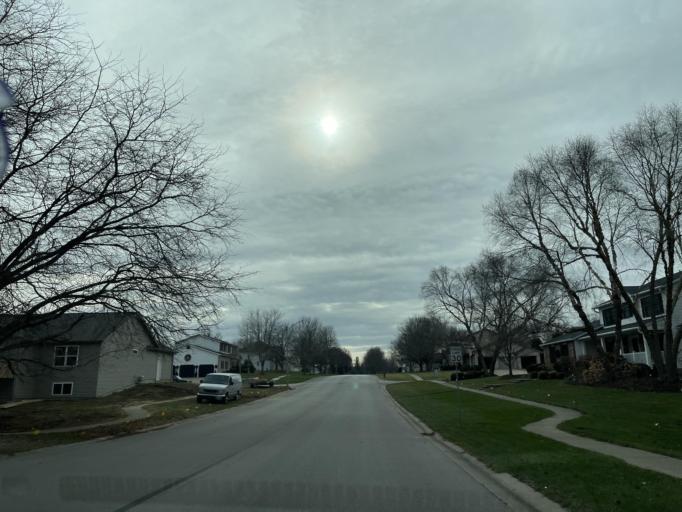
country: US
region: Illinois
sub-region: Sangamon County
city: Leland Grove
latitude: 39.7856
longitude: -89.7289
